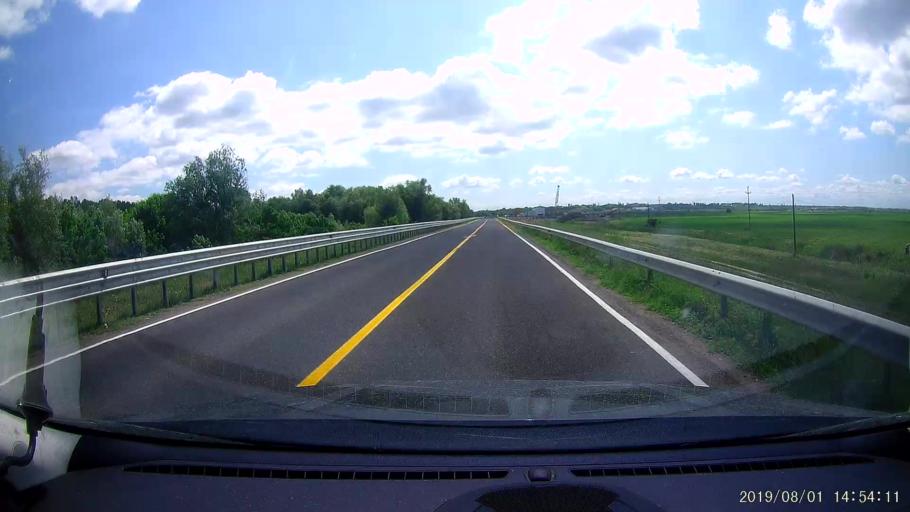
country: RO
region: Braila
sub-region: Municipiul Braila
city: Braila
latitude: 45.3218
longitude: 27.9929
